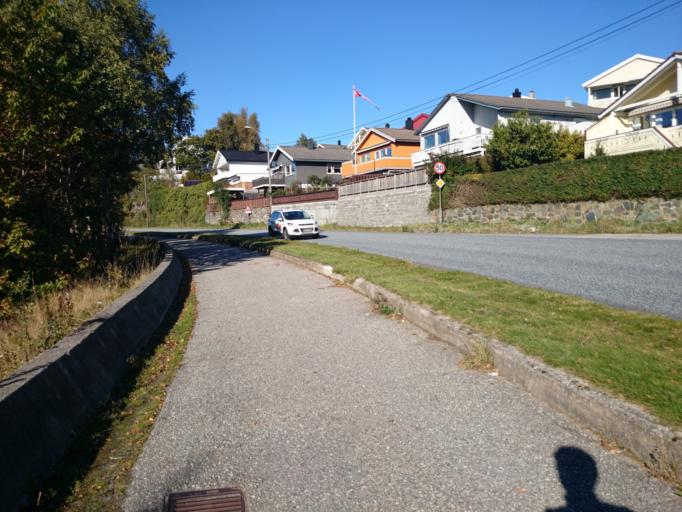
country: NO
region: Vest-Agder
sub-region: Kristiansand
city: Tveit
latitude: 58.1786
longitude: 8.0932
